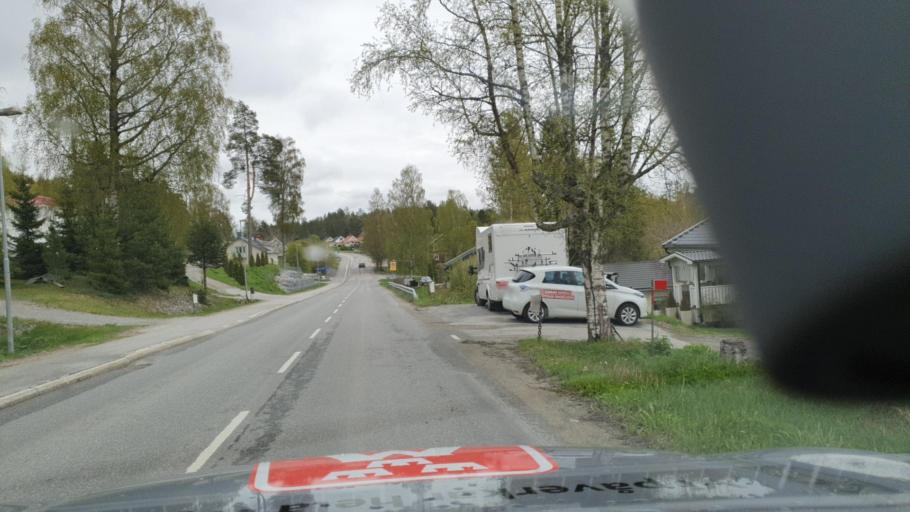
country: SE
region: Vaesternorrland
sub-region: OErnskoeldsviks Kommun
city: Ornskoldsvik
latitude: 63.3048
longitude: 18.5832
